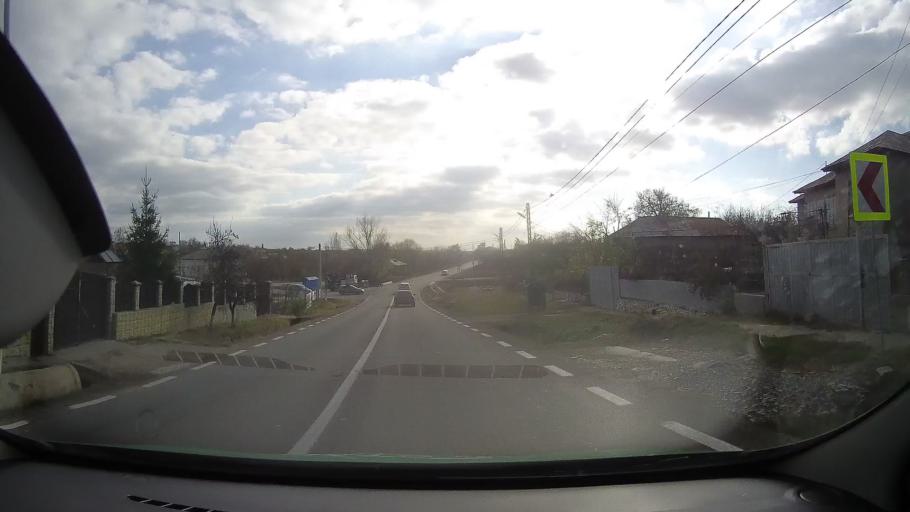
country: RO
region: Tulcea
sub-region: Comuna Topolog
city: Topolog
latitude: 44.8761
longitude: 28.3739
